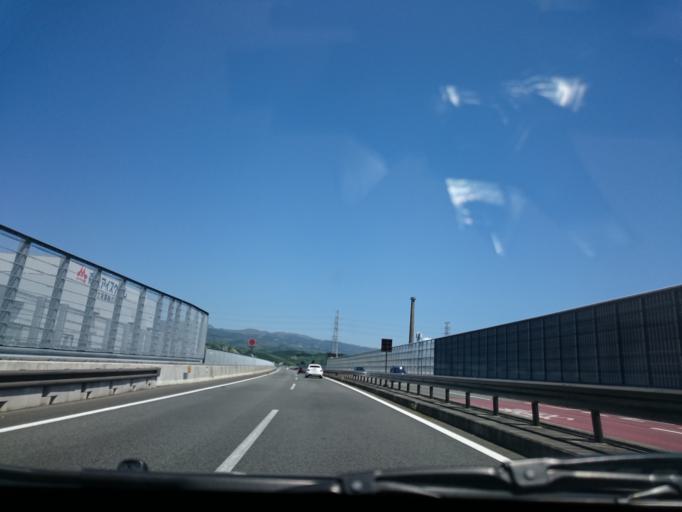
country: JP
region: Shizuoka
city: Mishima
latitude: 35.1495
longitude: 138.8999
